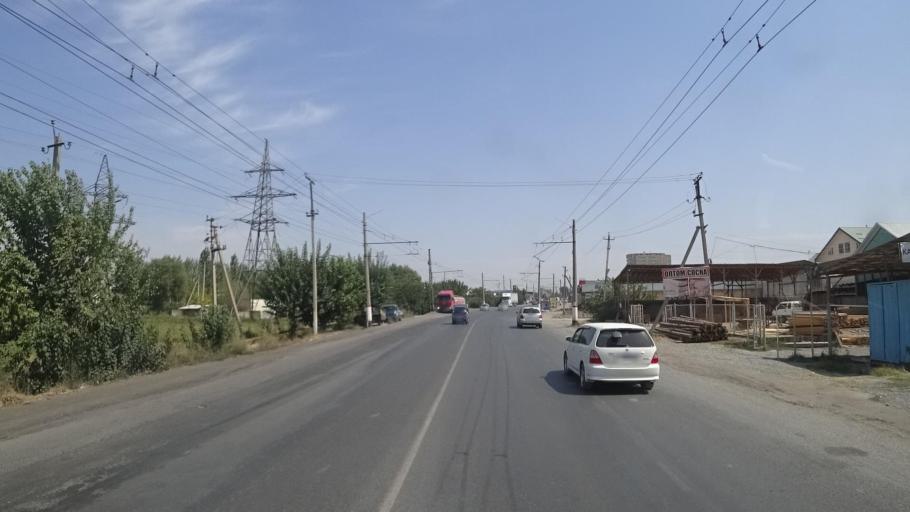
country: KG
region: Osh
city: Osh
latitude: 40.5678
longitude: 72.7935
